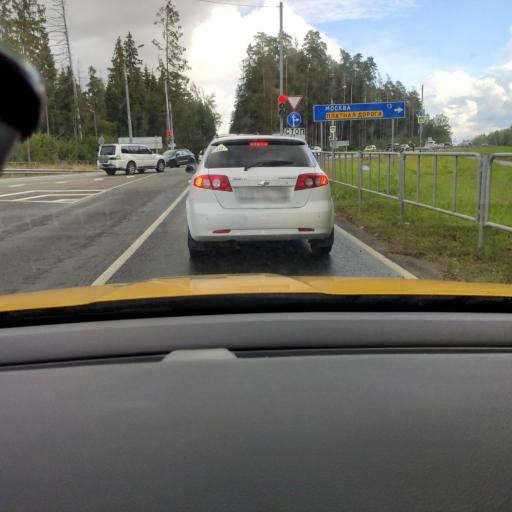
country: RU
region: Moskovskaya
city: Lesnoy Gorodok
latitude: 55.6738
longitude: 37.1783
